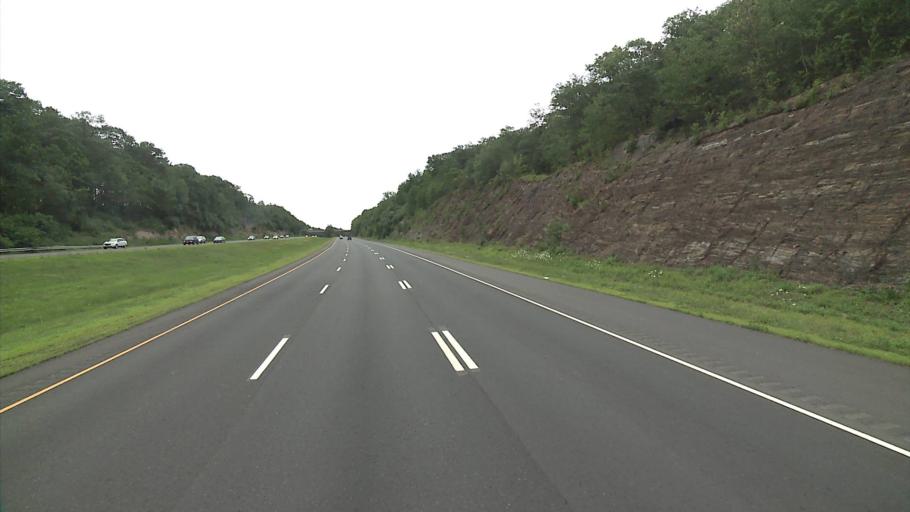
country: US
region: Connecticut
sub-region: Fairfield County
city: Shelton
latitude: 41.2787
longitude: -73.1135
